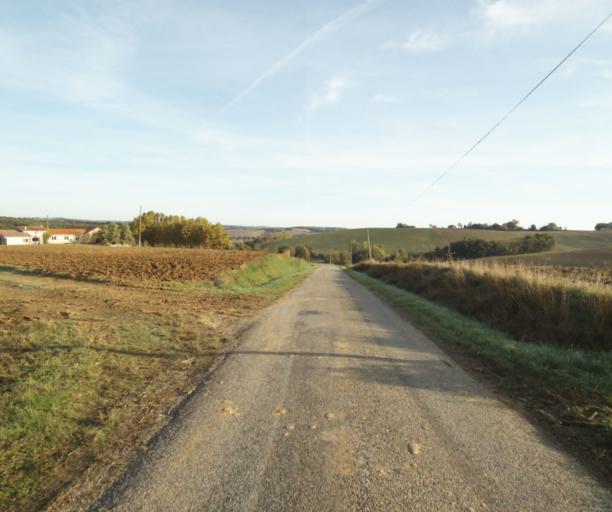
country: FR
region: Midi-Pyrenees
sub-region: Departement du Tarn-et-Garonne
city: Nohic
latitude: 43.9211
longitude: 1.4813
